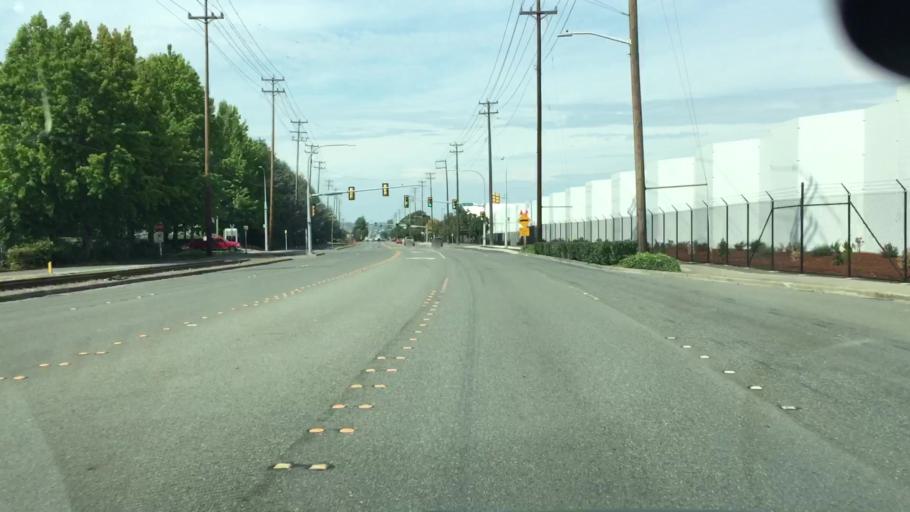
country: US
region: Washington
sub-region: King County
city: Boulevard Park
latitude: 47.5298
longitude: -122.3058
